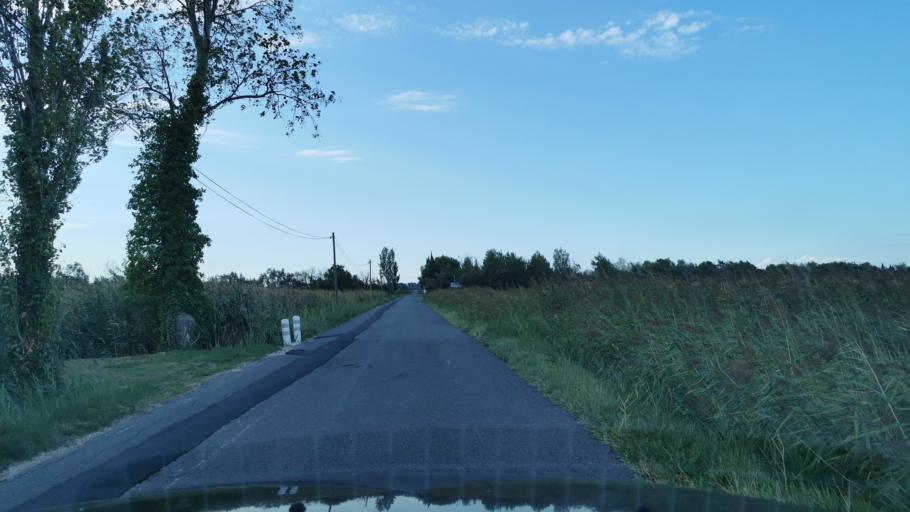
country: FR
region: Languedoc-Roussillon
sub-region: Departement de l'Aude
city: Narbonne
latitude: 43.1398
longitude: 3.0269
